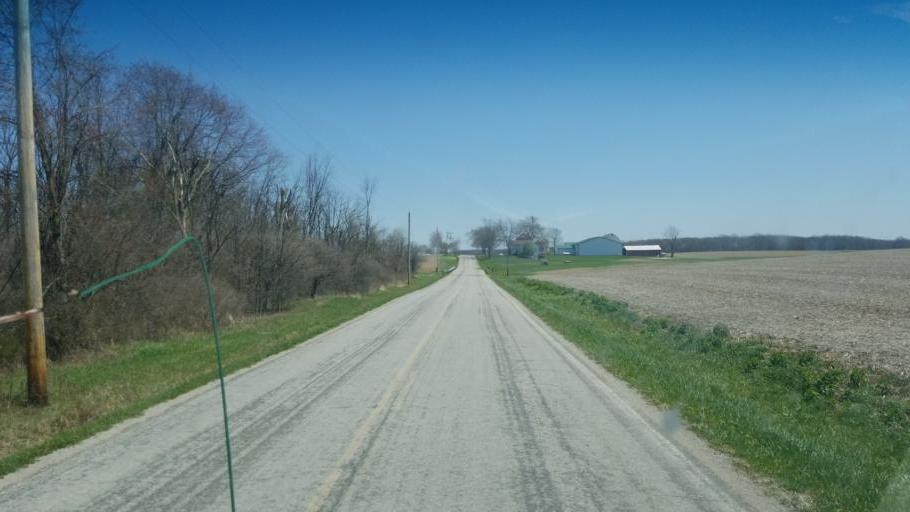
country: US
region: Ohio
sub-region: Huron County
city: New London
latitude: 41.1019
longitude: -82.3557
